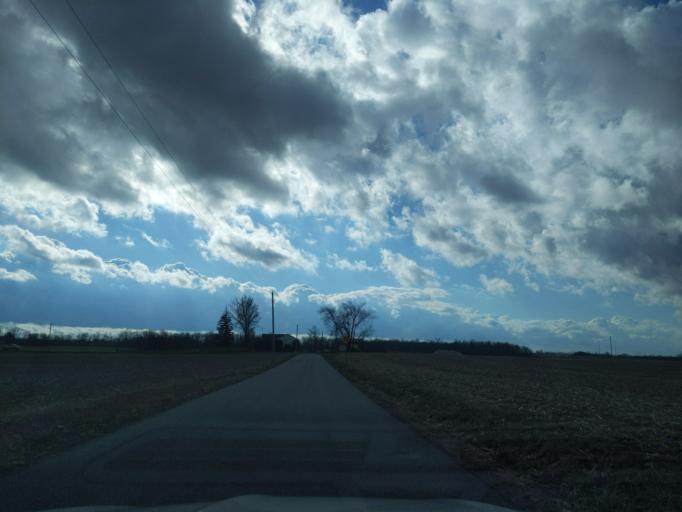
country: US
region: Indiana
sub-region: Decatur County
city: Greensburg
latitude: 39.3747
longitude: -85.5034
